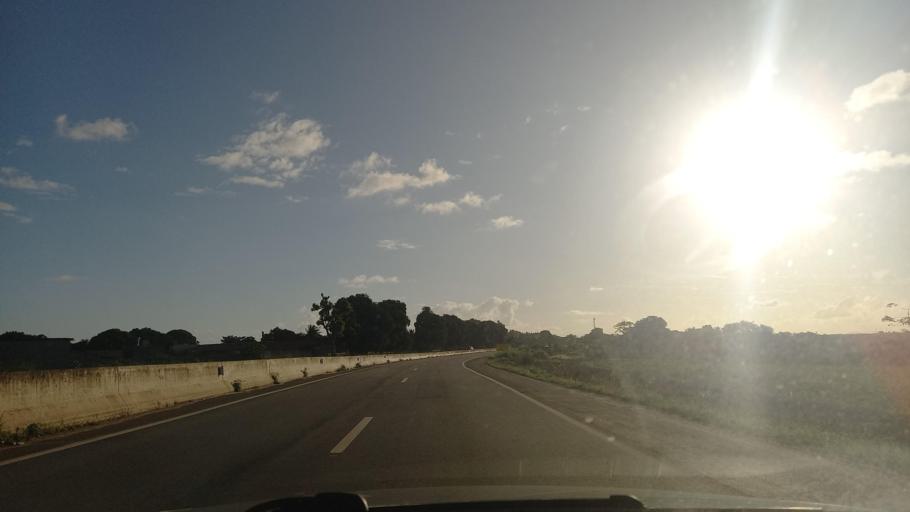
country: BR
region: Alagoas
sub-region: Campo Alegre
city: Campo Alegre
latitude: -9.8036
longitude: -36.2687
